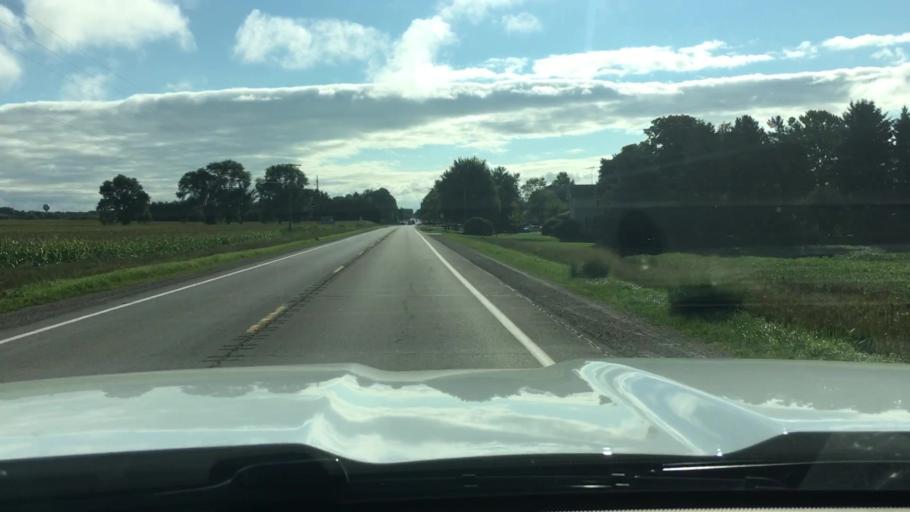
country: US
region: Michigan
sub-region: Tuscola County
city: Cass City
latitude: 43.6005
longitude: -83.1975
